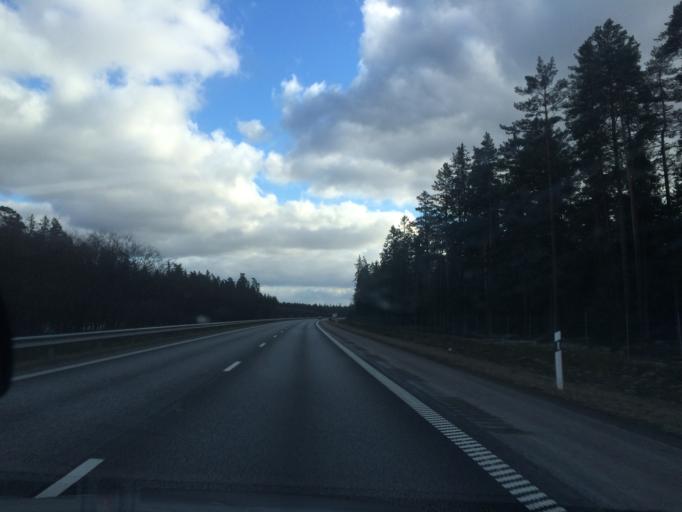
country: SE
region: Joenkoeping
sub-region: Vaggeryds Kommun
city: Skillingaryd
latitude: 57.3629
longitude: 14.1048
